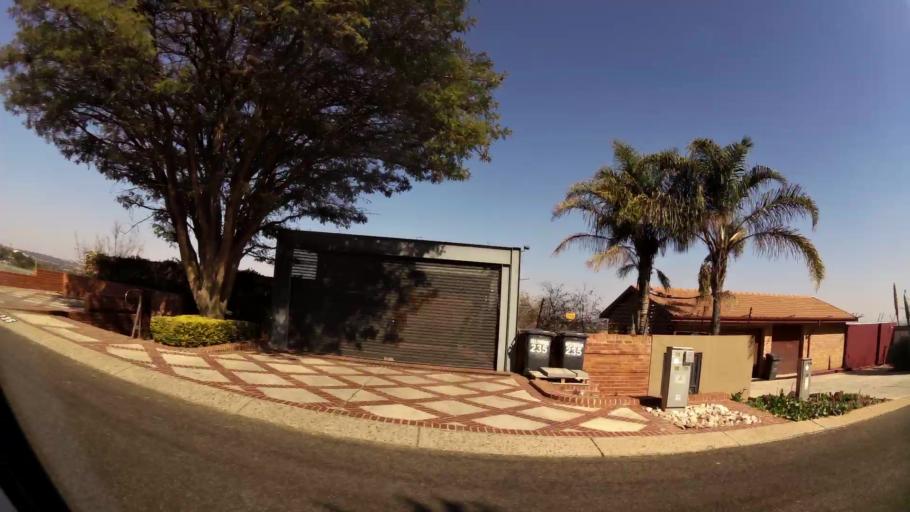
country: ZA
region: Gauteng
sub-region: City of Tshwane Metropolitan Municipality
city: Pretoria
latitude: -25.7947
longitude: 28.2353
